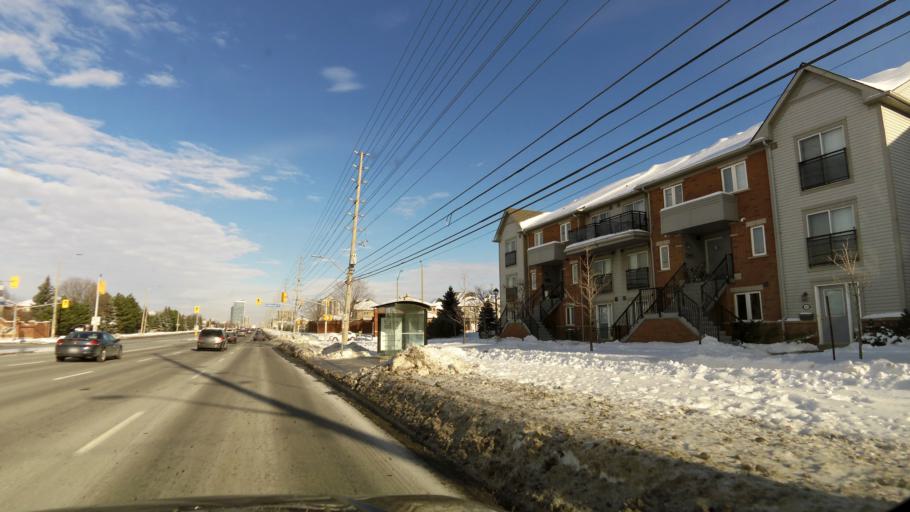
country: CA
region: Ontario
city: Mississauga
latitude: 43.5943
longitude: -79.6669
